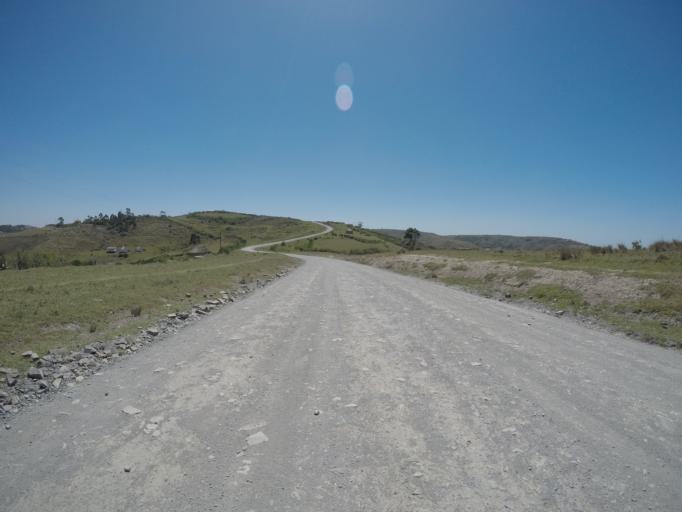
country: ZA
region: Eastern Cape
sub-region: OR Tambo District Municipality
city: Libode
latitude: -31.9802
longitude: 29.0351
